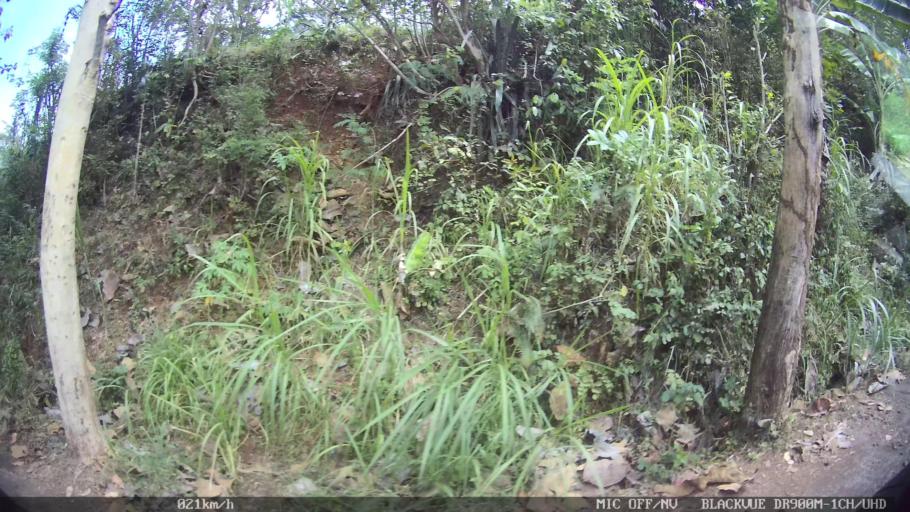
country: ID
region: Central Java
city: Candi Prambanan
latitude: -7.8179
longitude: 110.5249
